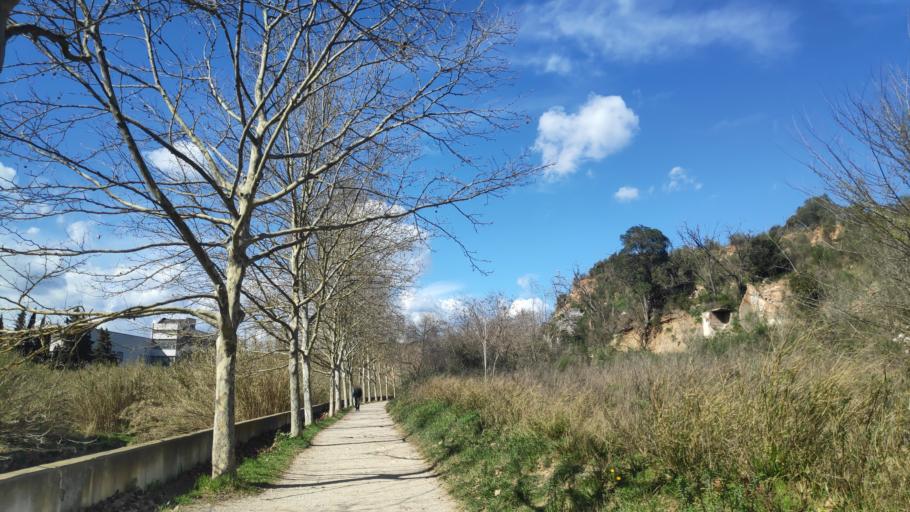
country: ES
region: Catalonia
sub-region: Provincia de Barcelona
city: Sabadell
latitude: 41.5581
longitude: 2.1146
